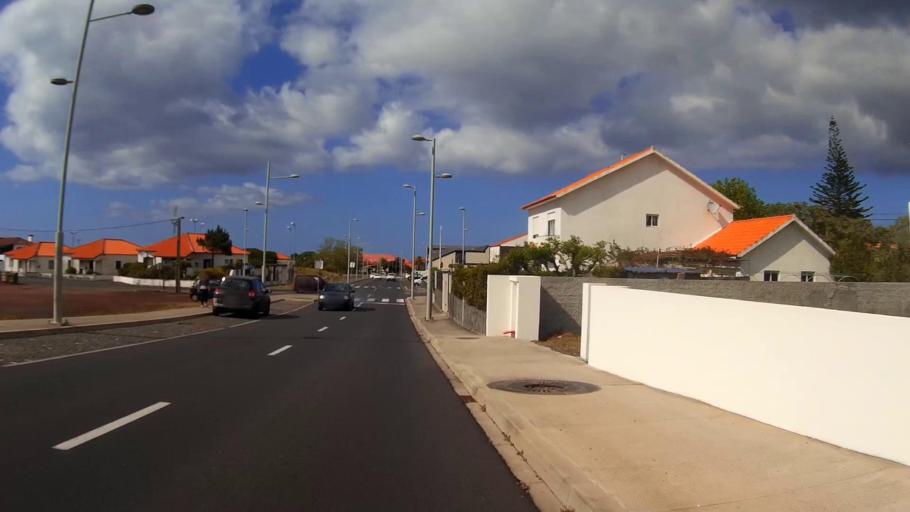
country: PT
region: Azores
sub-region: Madalena
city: Madalena
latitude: 38.5323
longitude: -28.5258
